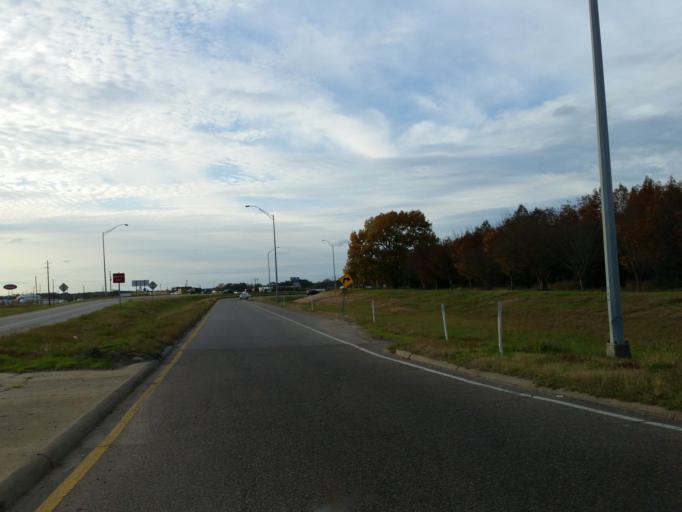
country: US
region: Mississippi
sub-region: Lauderdale County
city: Meridian
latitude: 32.3486
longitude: -88.7358
